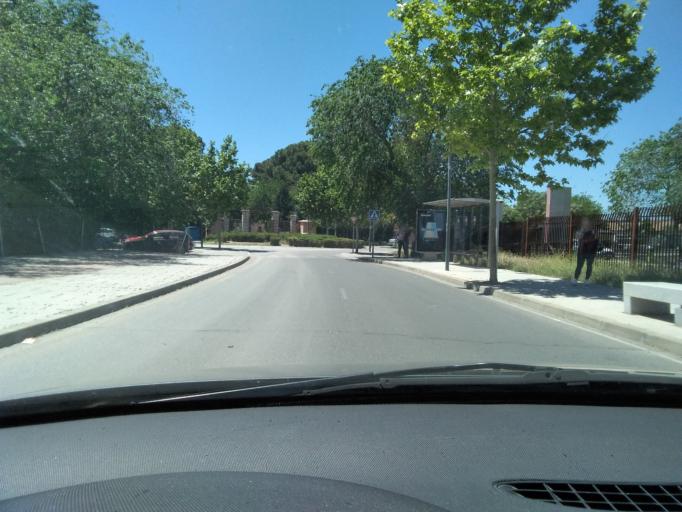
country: ES
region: Castille-La Mancha
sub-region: Province of Toledo
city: Toledo
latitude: 39.8665
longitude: -4.0405
